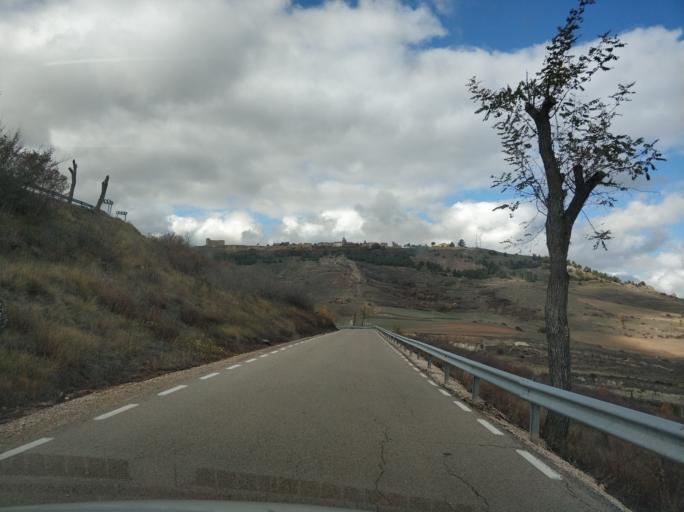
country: ES
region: Castille and Leon
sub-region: Provincia de Soria
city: Medinaceli
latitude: 41.1633
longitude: -2.4257
